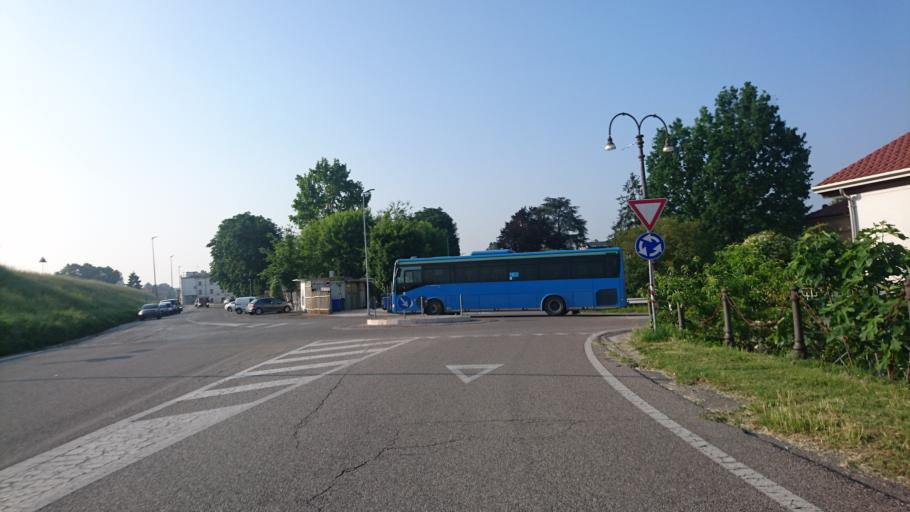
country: IT
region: Lombardy
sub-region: Provincia di Mantova
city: Sermide
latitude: 45.0092
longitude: 11.2974
